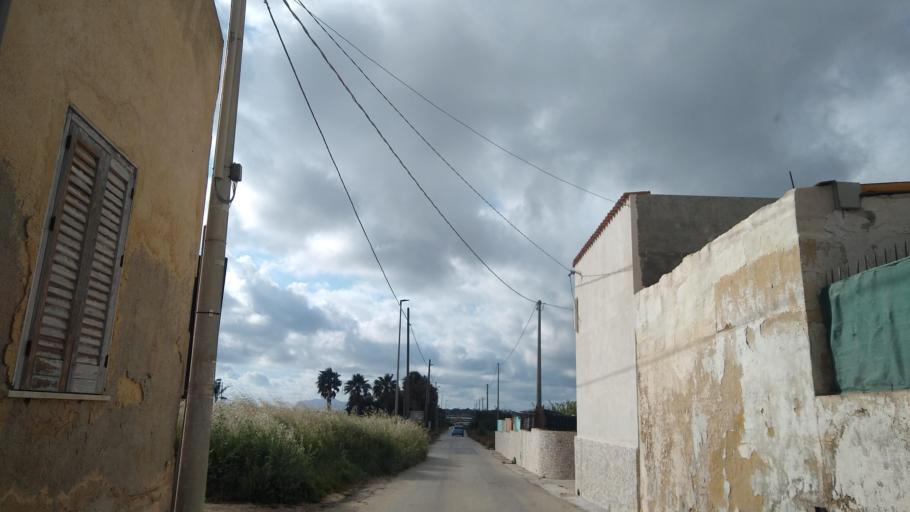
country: IT
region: Sicily
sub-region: Trapani
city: Marsala
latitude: 37.8558
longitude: 12.4868
